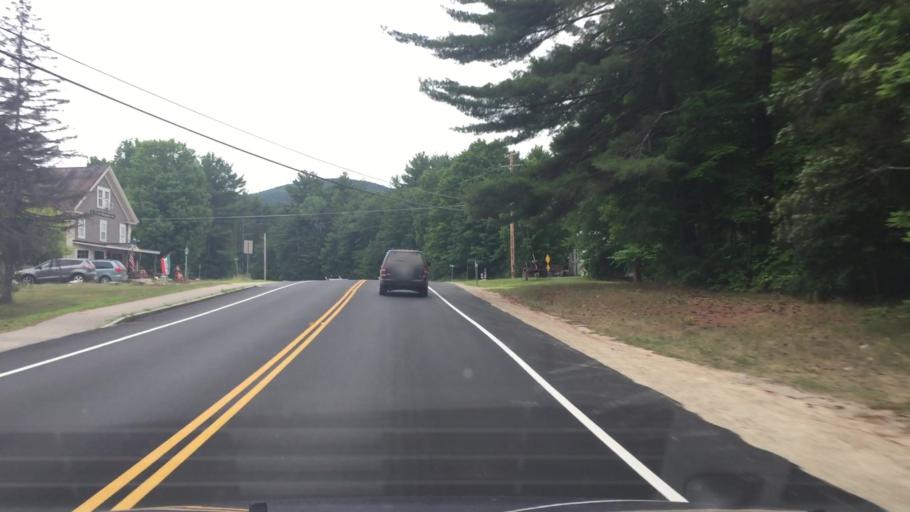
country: US
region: New Hampshire
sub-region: Carroll County
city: Freedom
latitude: 43.7957
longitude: -71.0559
